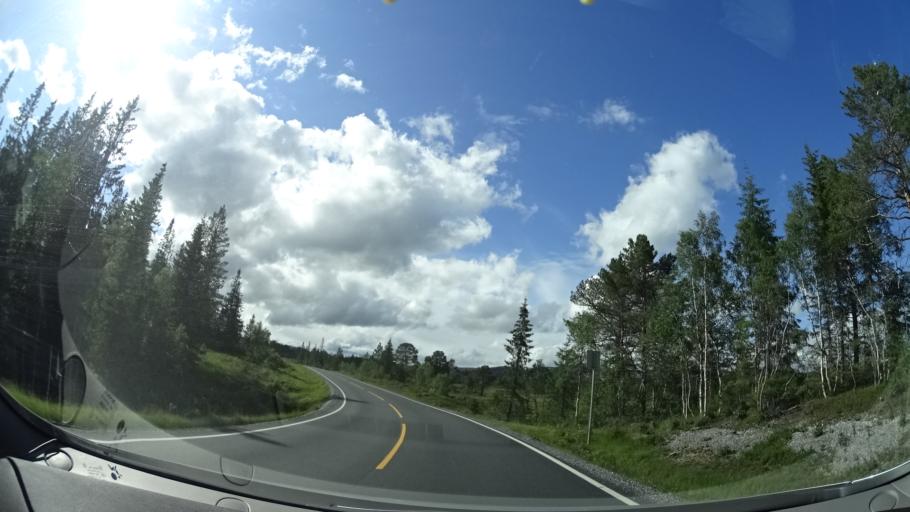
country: NO
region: Sor-Trondelag
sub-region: Snillfjord
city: Krokstadora
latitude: 63.2333
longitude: 9.5599
